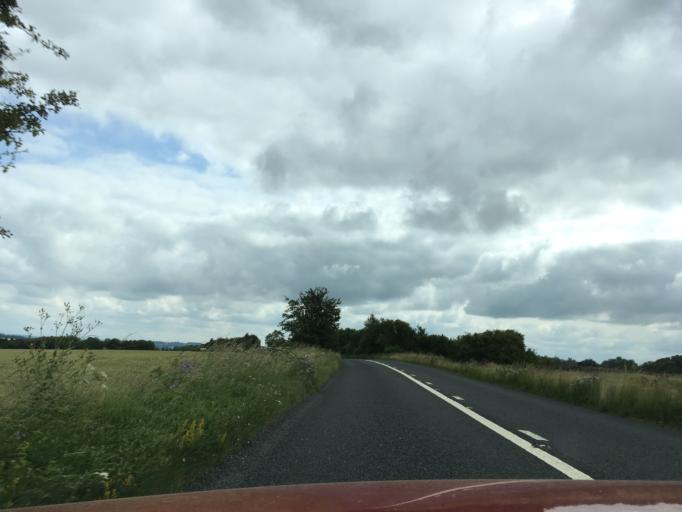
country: GB
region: England
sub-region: Gloucestershire
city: Westfield
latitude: 51.8870
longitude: -1.8295
